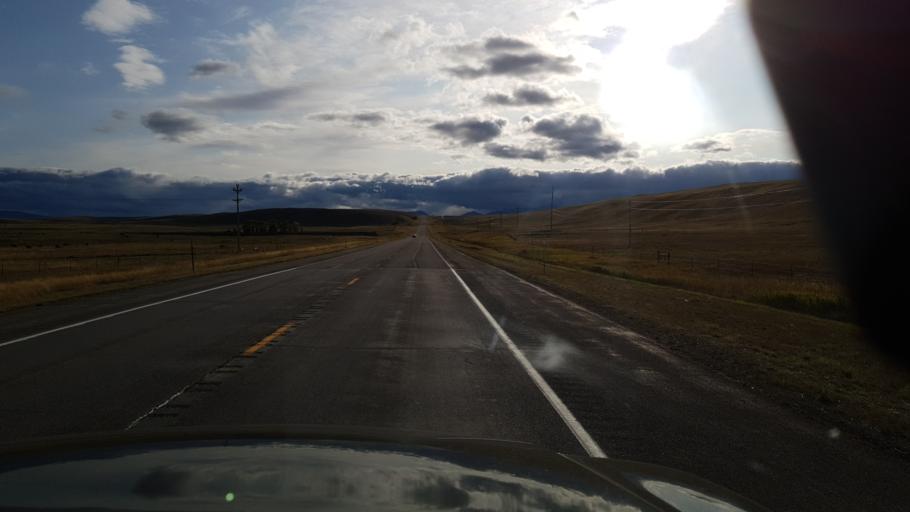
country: US
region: Montana
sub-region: Glacier County
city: South Browning
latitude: 48.5282
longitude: -113.0599
